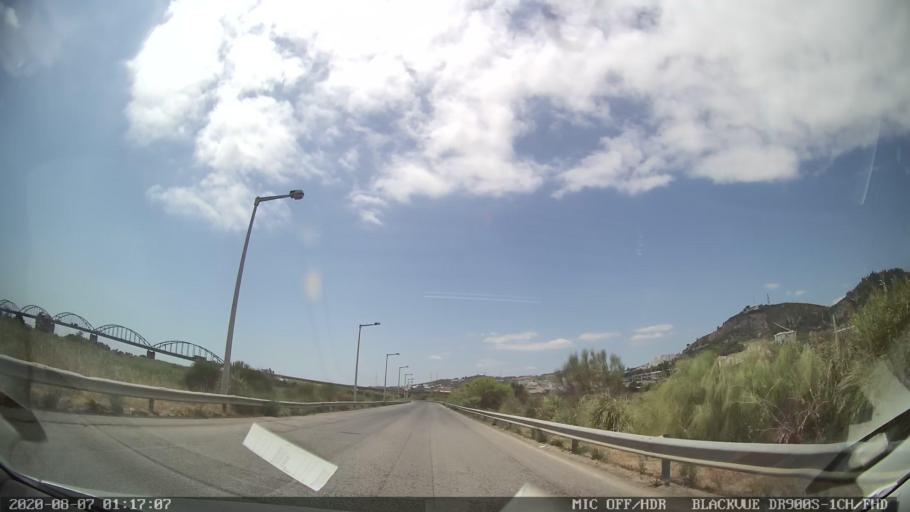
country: PT
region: Lisbon
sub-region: Vila Franca de Xira
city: Vila Franca de Xira
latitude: 38.9612
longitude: -8.9795
